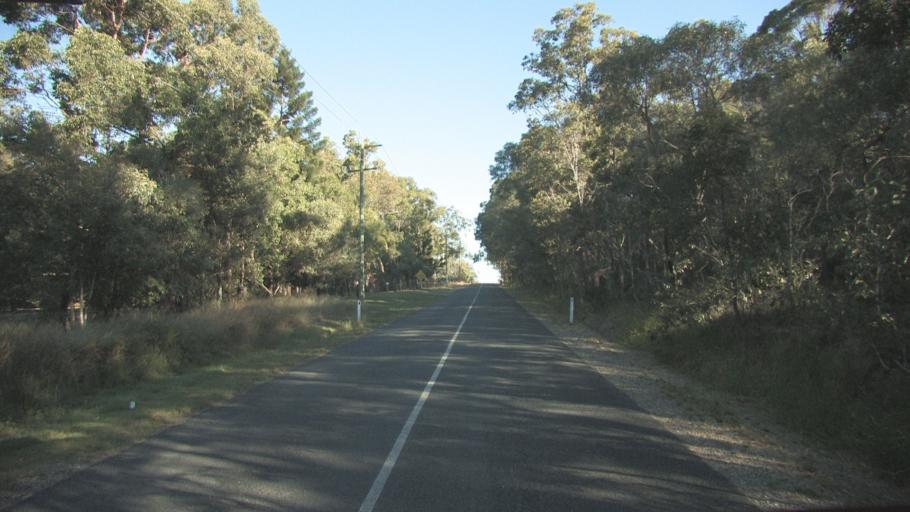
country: AU
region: Queensland
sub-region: Logan
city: Chambers Flat
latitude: -27.7620
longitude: 153.1232
